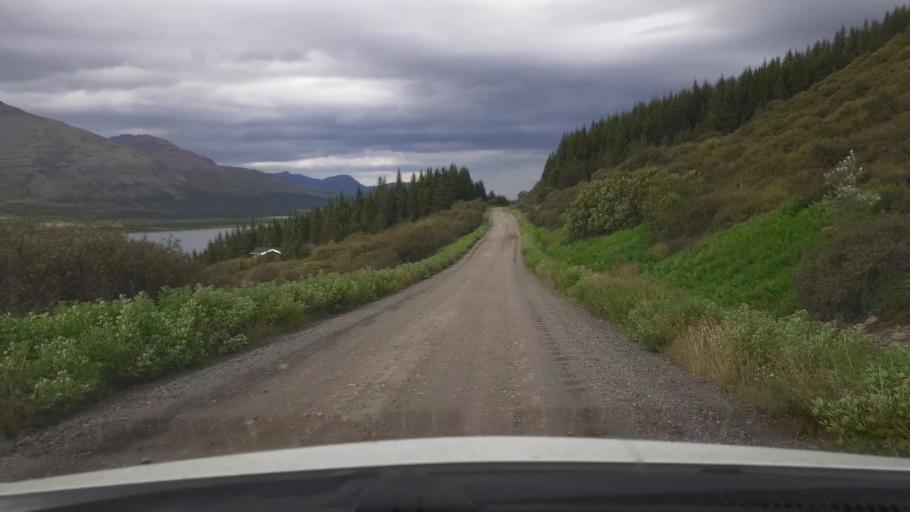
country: IS
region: Capital Region
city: Mosfellsbaer
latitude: 64.5276
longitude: -21.4959
